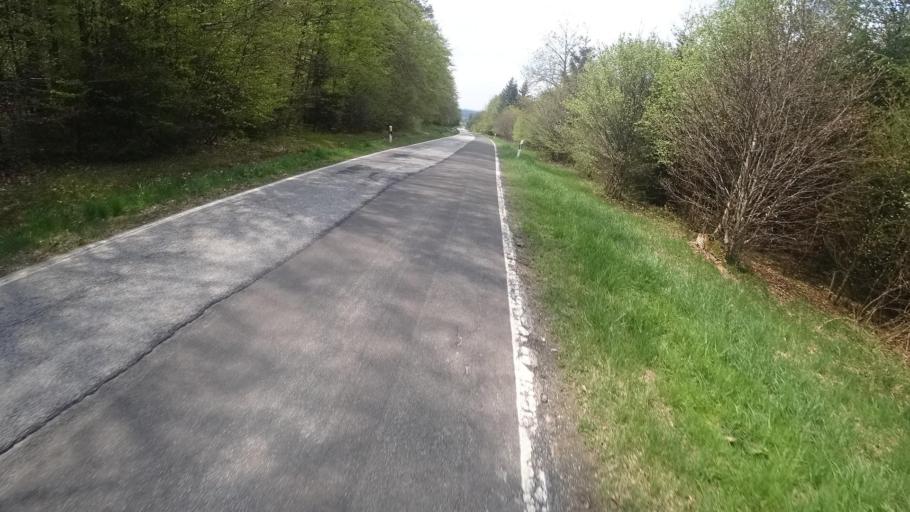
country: DE
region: Rheinland-Pfalz
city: Maisborn
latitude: 50.0791
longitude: 7.5734
